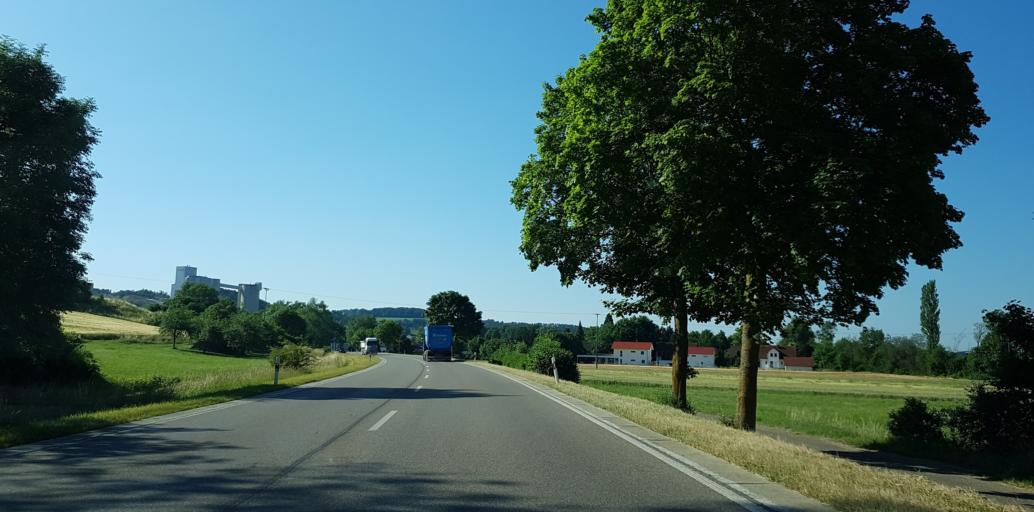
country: DE
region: Baden-Wuerttemberg
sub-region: Tuebingen Region
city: Allmendingen
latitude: 48.3384
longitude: 9.7223
